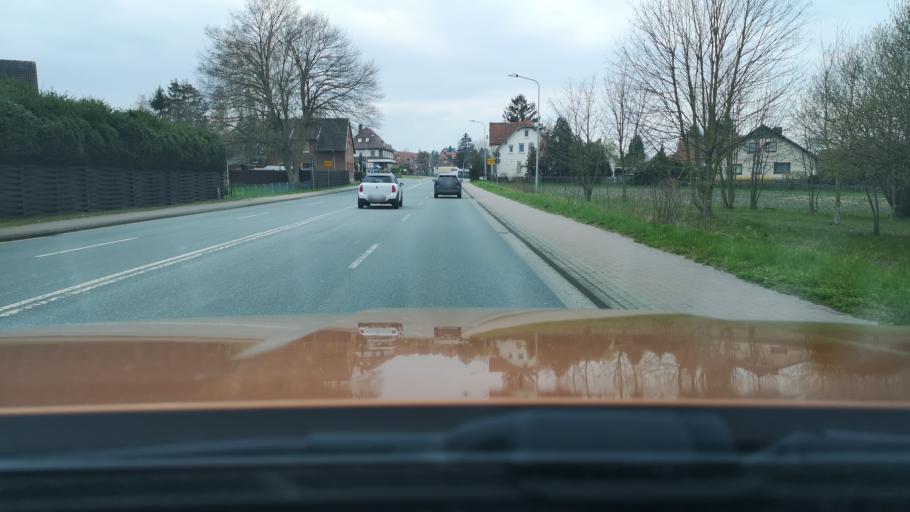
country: DE
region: Lower Saxony
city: Nienstadt
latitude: 52.2943
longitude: 9.1699
